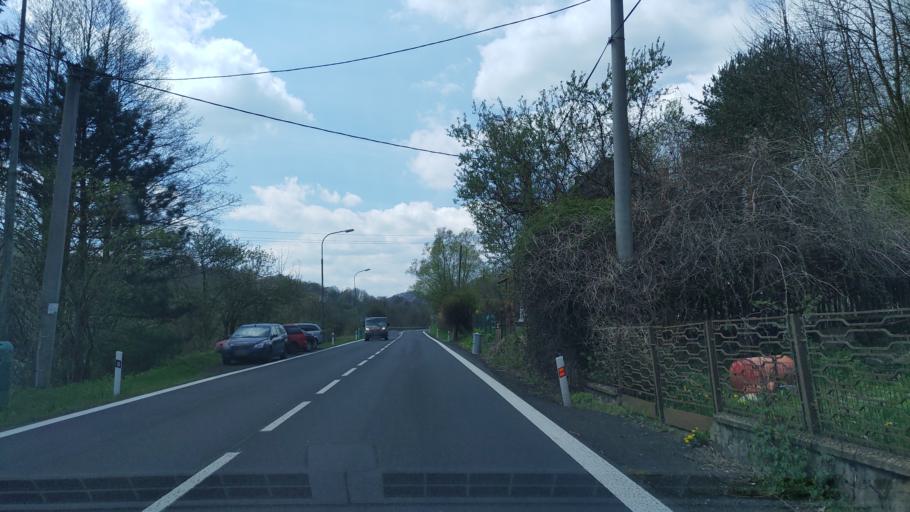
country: CZ
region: Ustecky
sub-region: Okres Chomutov
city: Perstejn
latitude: 50.3341
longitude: 13.0439
